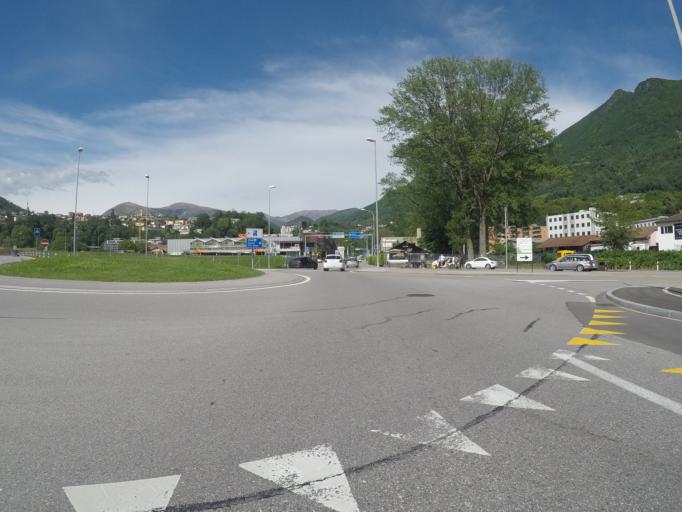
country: CH
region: Ticino
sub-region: Lugano District
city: Canobbio
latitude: 46.0266
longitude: 8.9657
